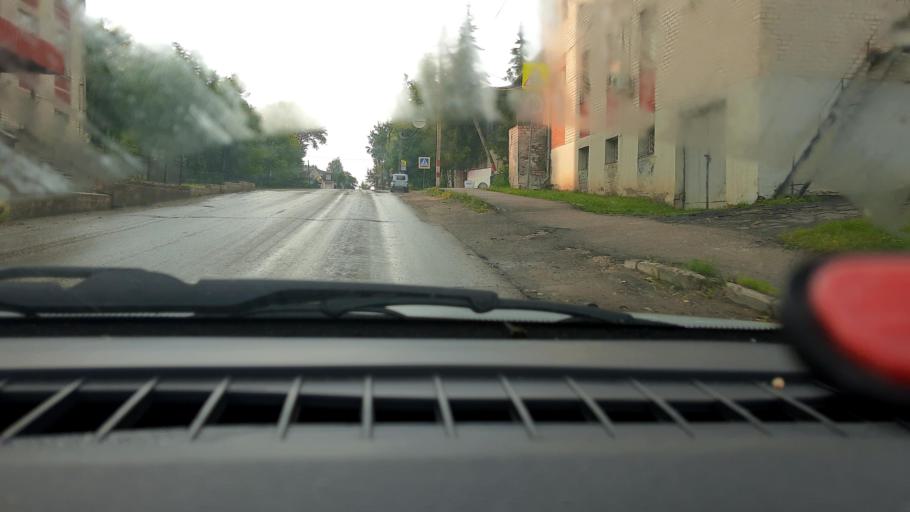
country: RU
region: Nizjnij Novgorod
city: Lukoyanov
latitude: 55.0336
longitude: 44.4949
